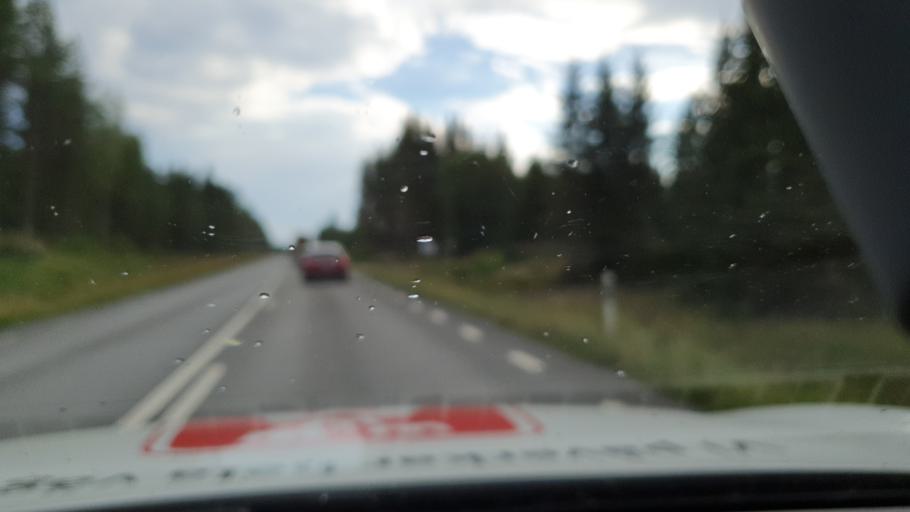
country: SE
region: Jaemtland
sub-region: Stroemsunds Kommun
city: Stroemsund
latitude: 63.5329
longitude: 15.3335
